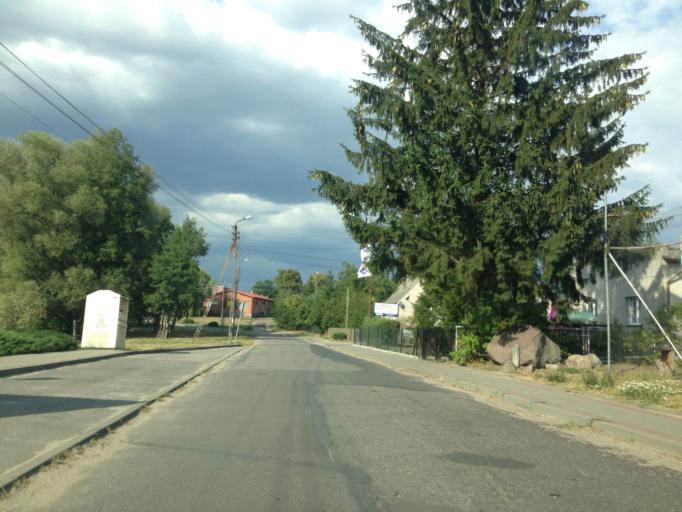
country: PL
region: Kujawsko-Pomorskie
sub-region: Powiat swiecki
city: Swiekatowo
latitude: 53.4884
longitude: 18.1390
